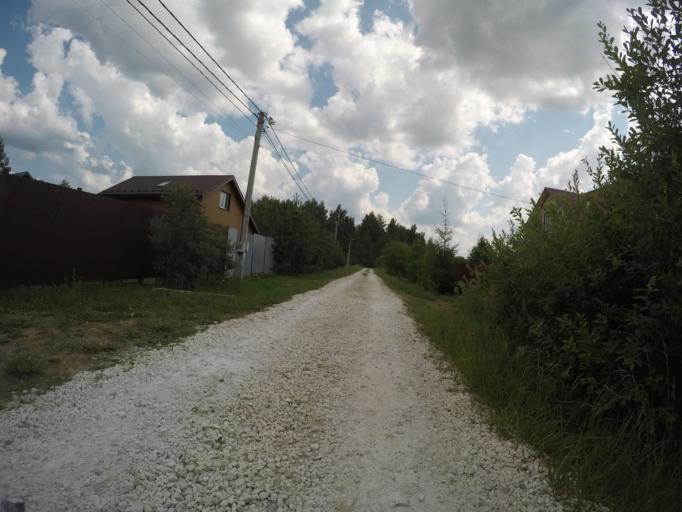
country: RU
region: Moskovskaya
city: Rechitsy
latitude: 55.6063
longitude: 38.5055
